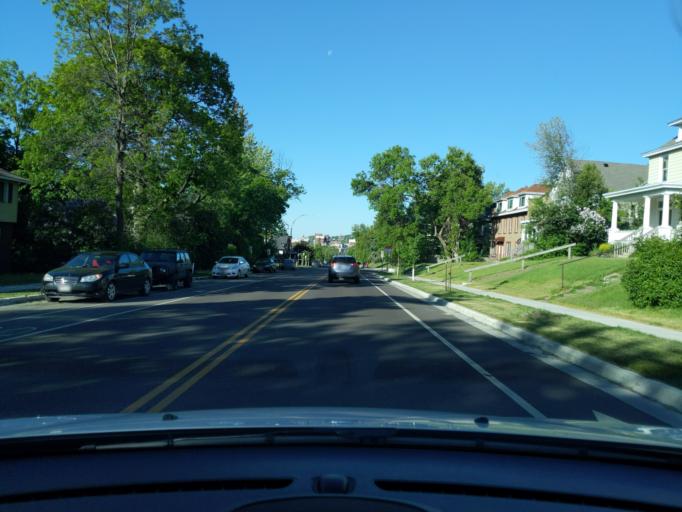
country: US
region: Minnesota
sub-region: Saint Louis County
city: Duluth
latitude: 46.8056
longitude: -92.0818
